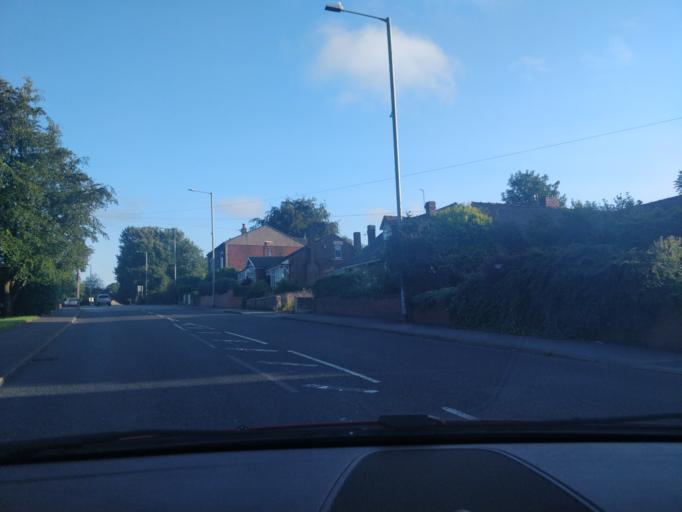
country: GB
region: England
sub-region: Lancashire
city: Appley Bridge
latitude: 53.5466
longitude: -2.7265
